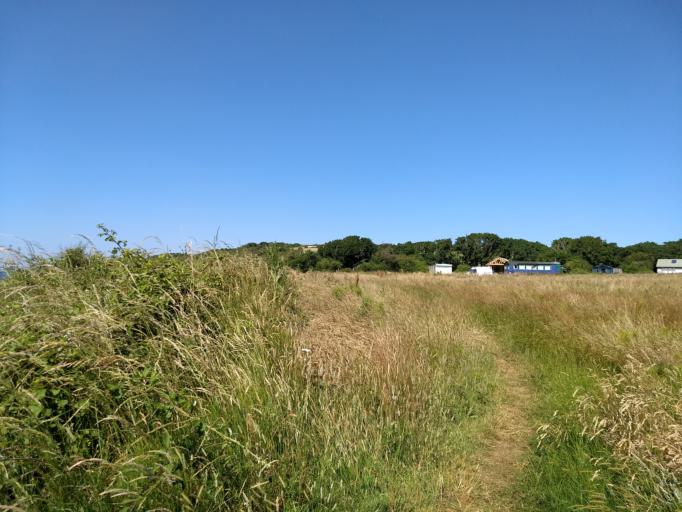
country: GB
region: England
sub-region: Isle of Wight
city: Gurnard
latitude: 50.7421
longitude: -1.3482
